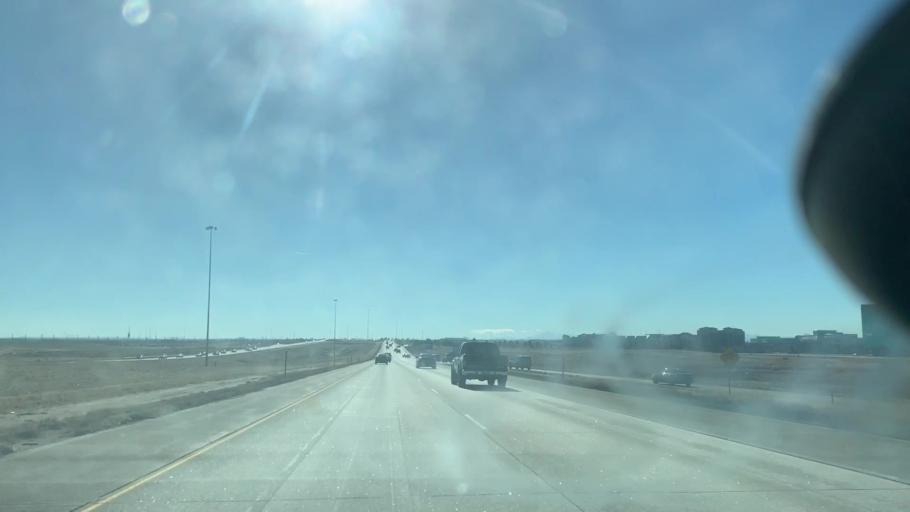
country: US
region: Colorado
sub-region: Adams County
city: Aurora
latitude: 39.7814
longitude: -104.7914
